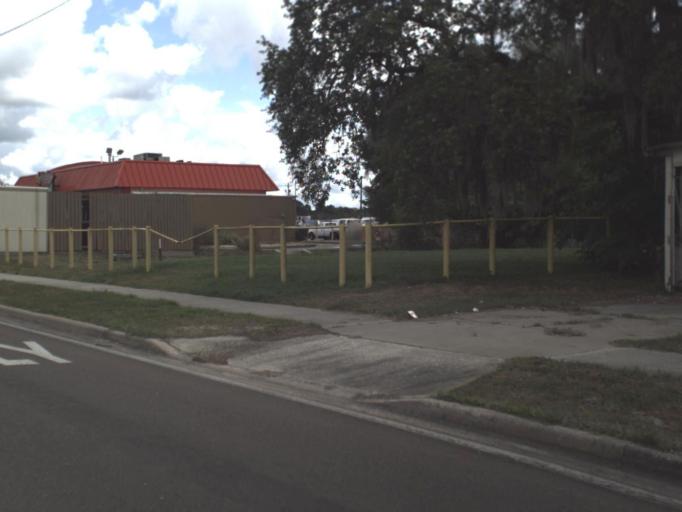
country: US
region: Florida
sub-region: Polk County
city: Winston
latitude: 28.0536
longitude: -81.9901
